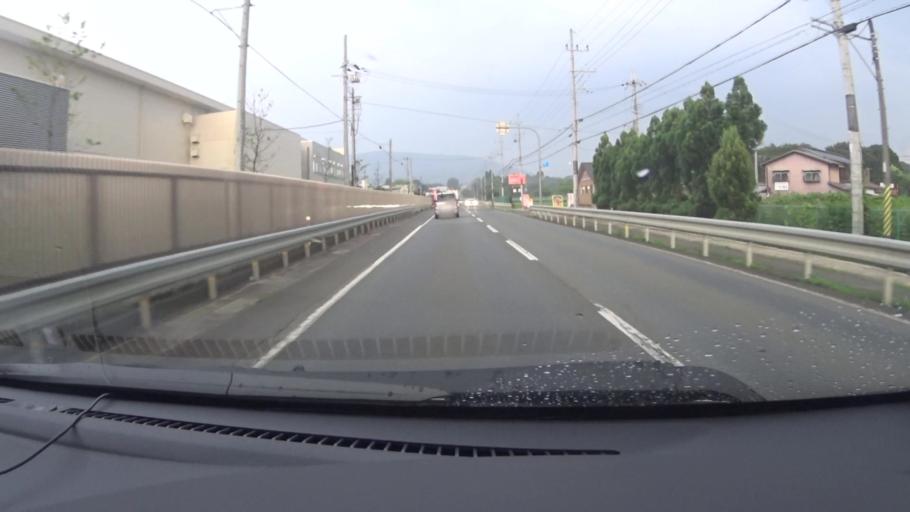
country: JP
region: Kyoto
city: Ayabe
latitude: 35.1795
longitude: 135.4211
